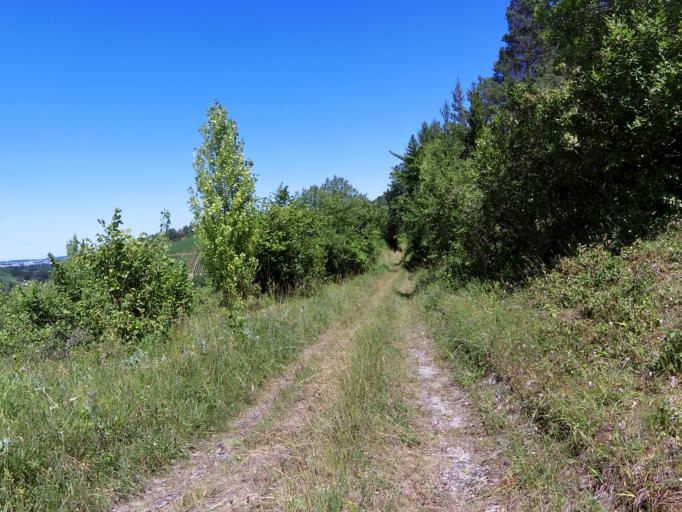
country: DE
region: Bavaria
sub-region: Regierungsbezirk Unterfranken
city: Randersacker
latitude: 49.7595
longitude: 9.9914
